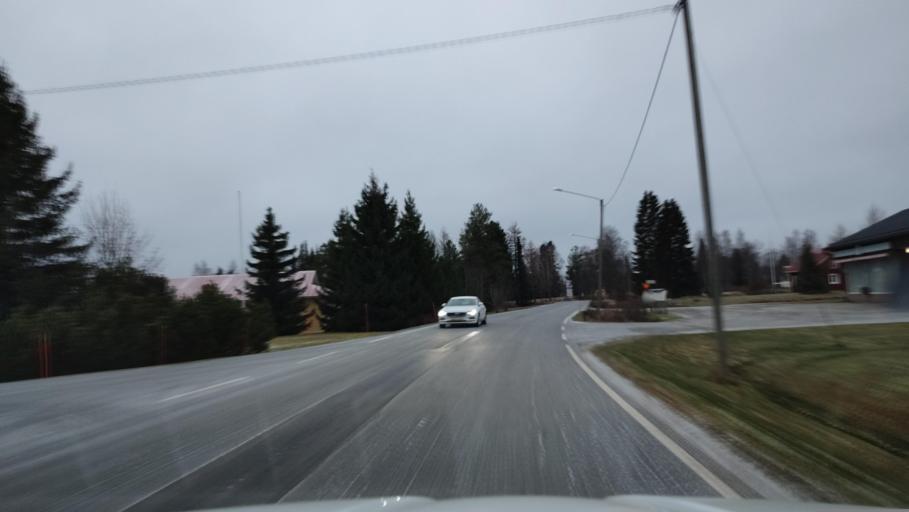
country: FI
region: Southern Ostrobothnia
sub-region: Suupohja
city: Karijoki
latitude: 62.2333
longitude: 21.6482
